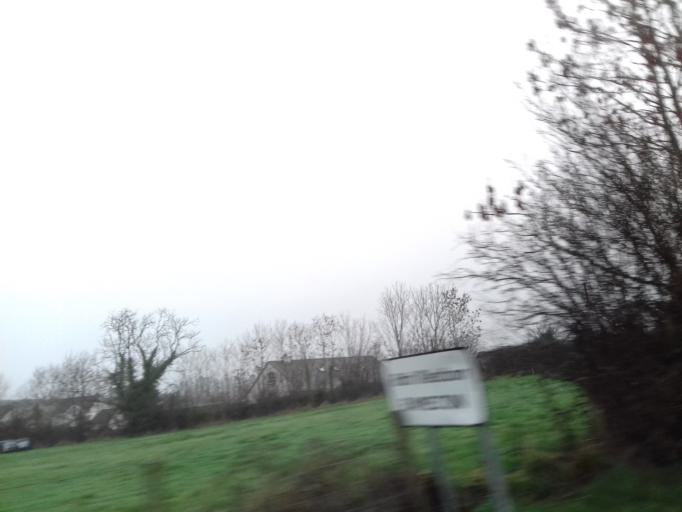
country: IE
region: Ulster
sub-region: County Donegal
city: Ramelton
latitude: 55.0298
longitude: -7.6485
